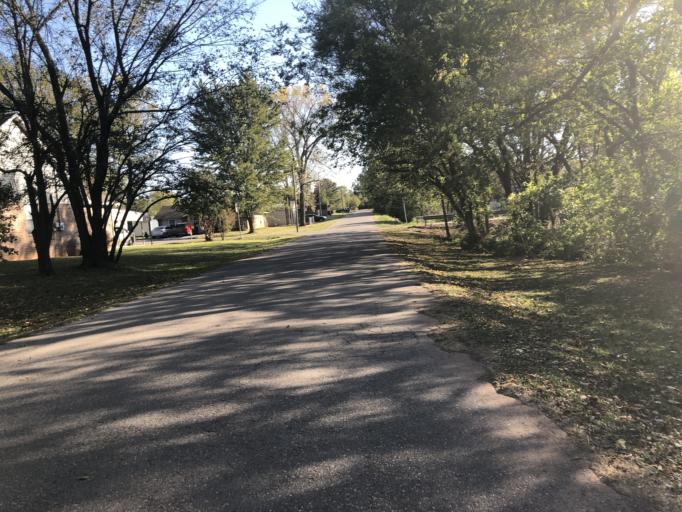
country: US
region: Oklahoma
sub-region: Pottawatomie County
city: Tecumseh
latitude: 35.2560
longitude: -96.9407
